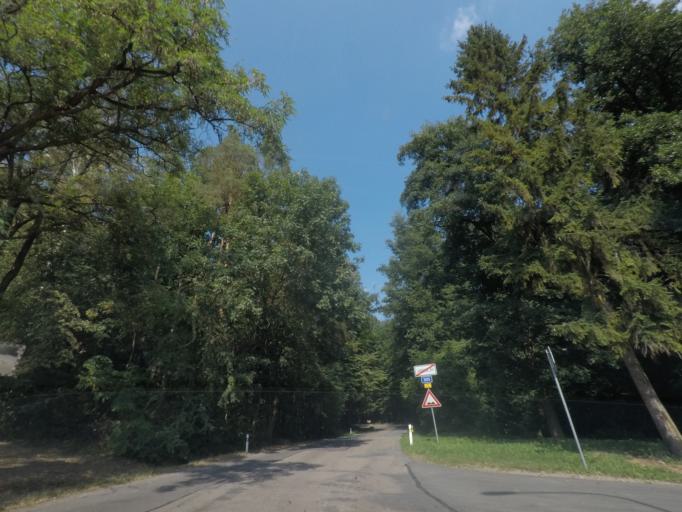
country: CZ
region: Pardubicky
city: Horni Jeleni
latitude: 50.0177
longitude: 16.0810
